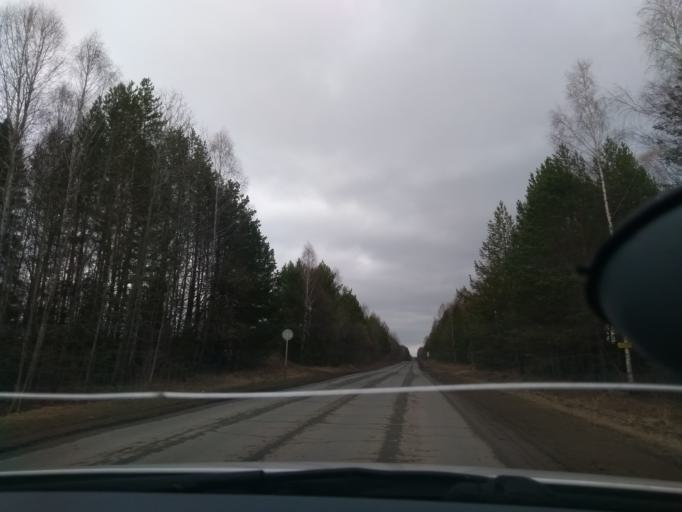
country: RU
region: Perm
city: Kungur
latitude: 57.3507
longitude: 56.7993
